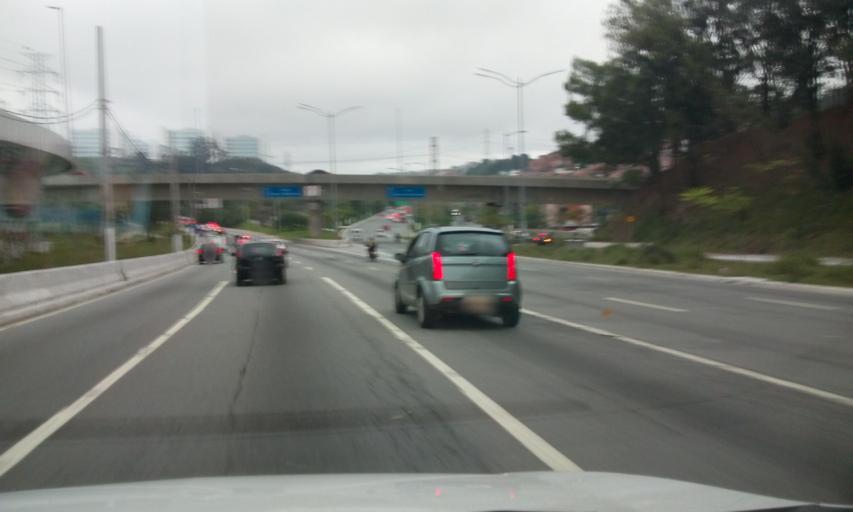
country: BR
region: Sao Paulo
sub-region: Taboao Da Serra
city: Taboao da Serra
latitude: -23.6404
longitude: -46.7262
